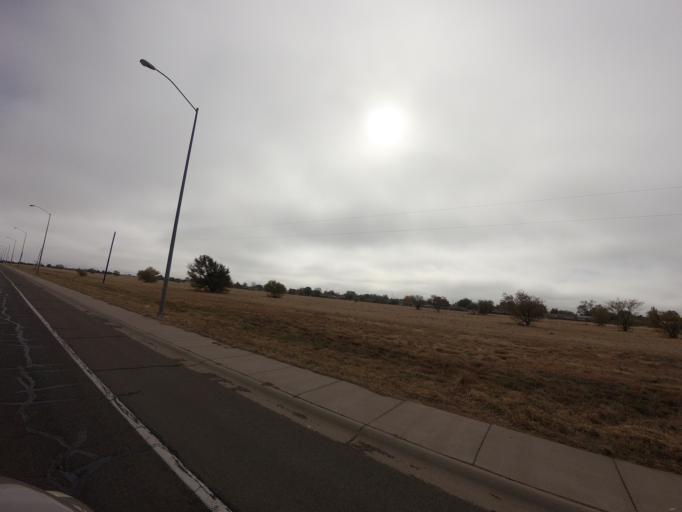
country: US
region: New Mexico
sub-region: Curry County
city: Clovis
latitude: 34.4340
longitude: -103.2219
